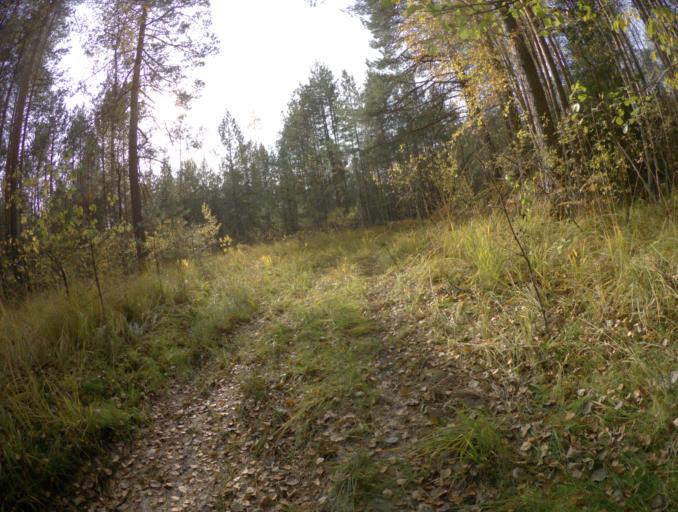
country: RU
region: Vladimir
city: Sobinka
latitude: 55.9343
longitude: 40.0408
